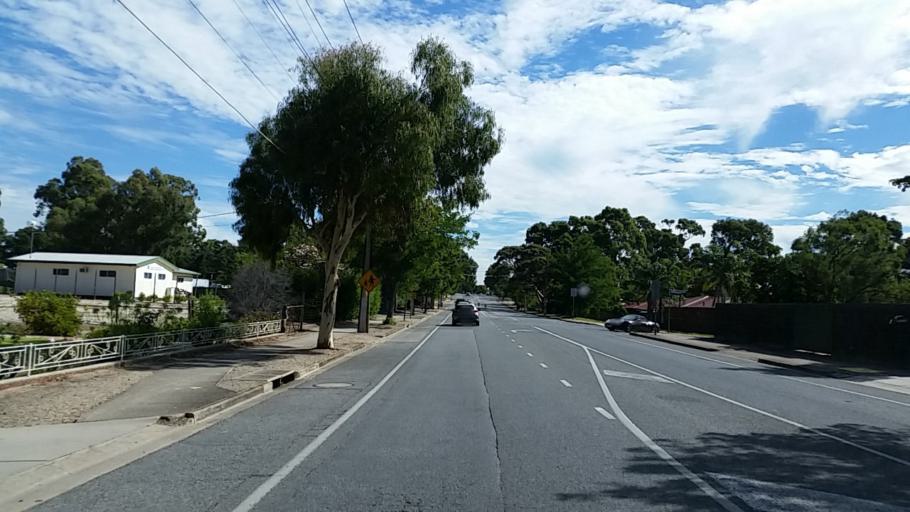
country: AU
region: South Australia
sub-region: Campbelltown
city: Athelstone
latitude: -34.8740
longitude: 138.6974
